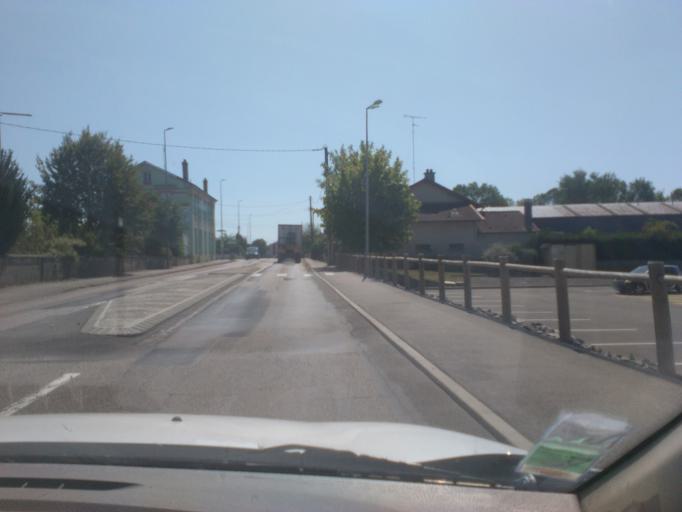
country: FR
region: Lorraine
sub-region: Departement des Vosges
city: Rambervillers
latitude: 48.3351
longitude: 6.6358
